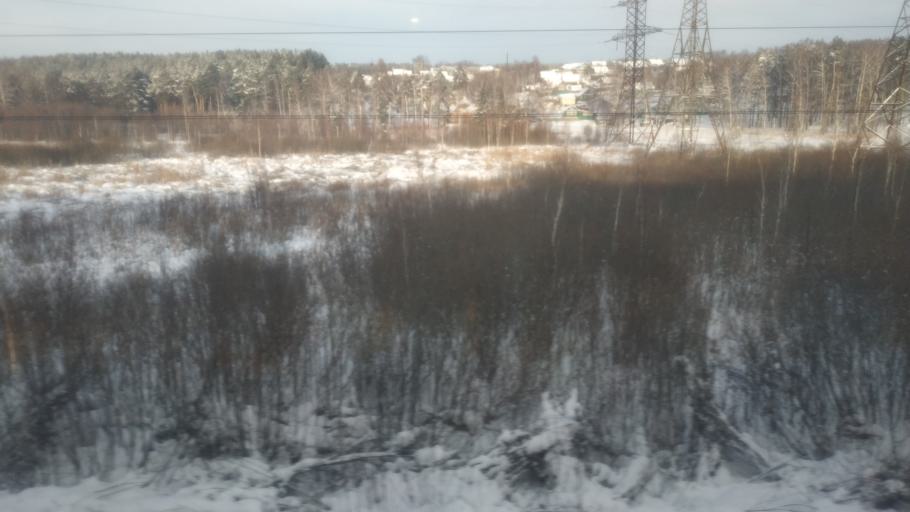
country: RU
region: Kirov
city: Krasnaya Polyana
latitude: 56.2522
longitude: 51.1423
